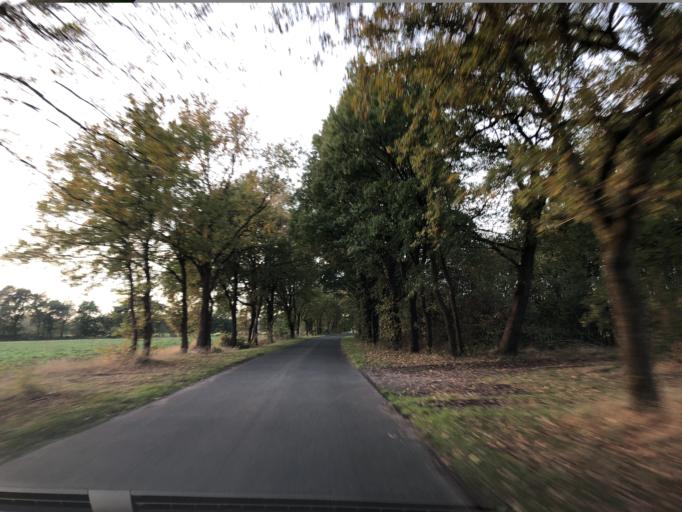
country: DE
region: Lower Saxony
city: Lehe
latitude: 53.0232
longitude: 7.3538
